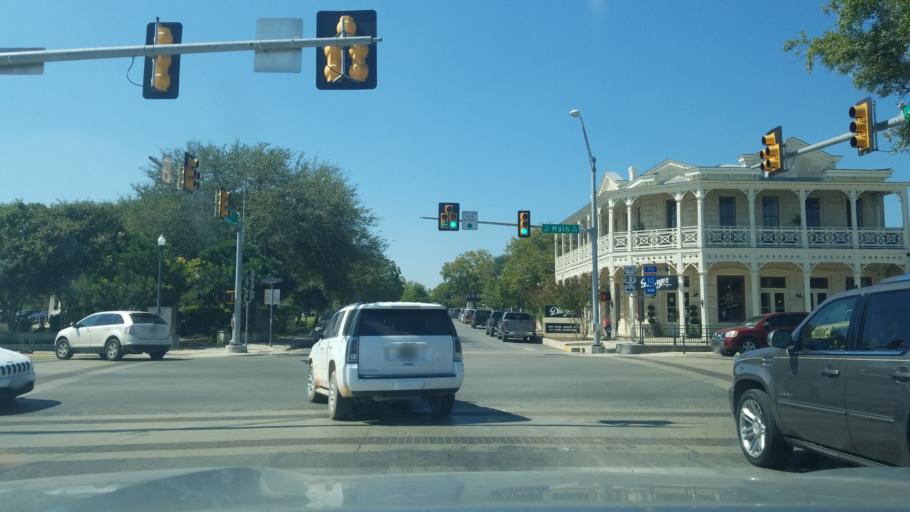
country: US
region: Texas
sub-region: Kendall County
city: Boerne
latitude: 29.7946
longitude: -98.7319
